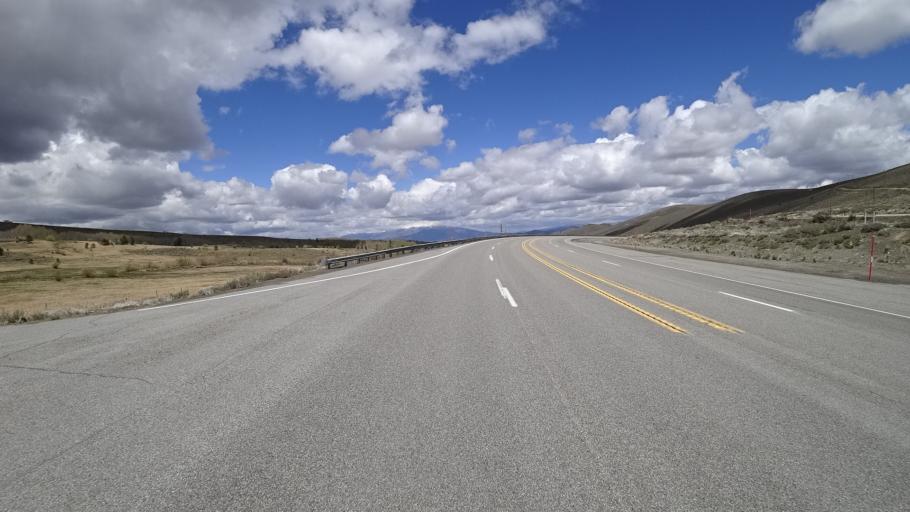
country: US
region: California
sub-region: Mono County
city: Bridgeport
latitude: 38.0879
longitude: -119.1823
